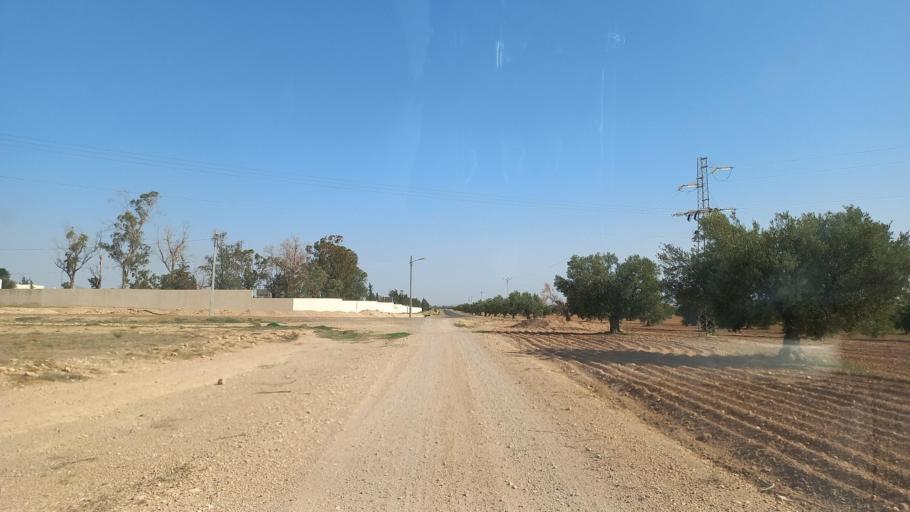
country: TN
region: Al Qasrayn
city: Kasserine
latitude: 35.2965
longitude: 9.0309
